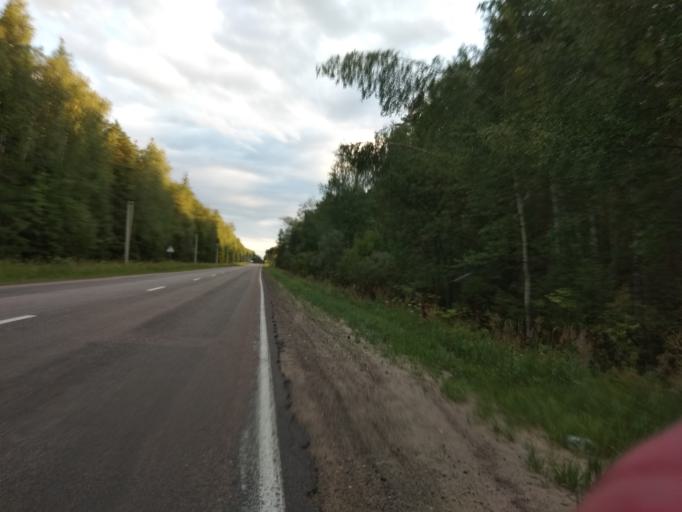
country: RU
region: Moskovskaya
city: Misheronskiy
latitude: 55.6230
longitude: 39.7317
